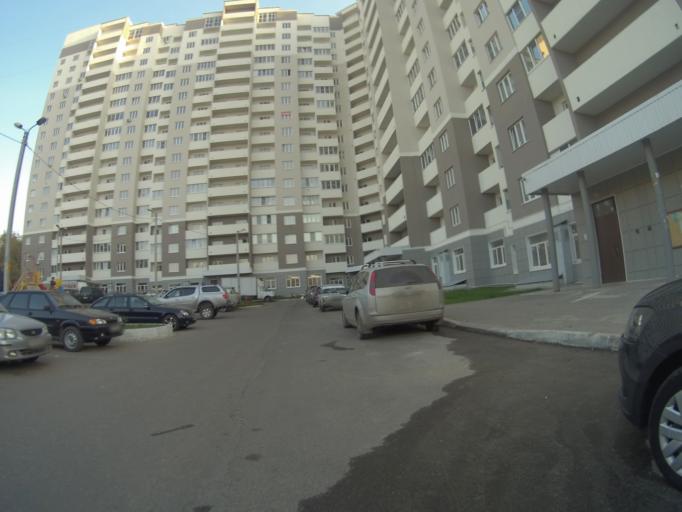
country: RU
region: Vladimir
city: Vladimir
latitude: 56.1194
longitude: 40.3462
